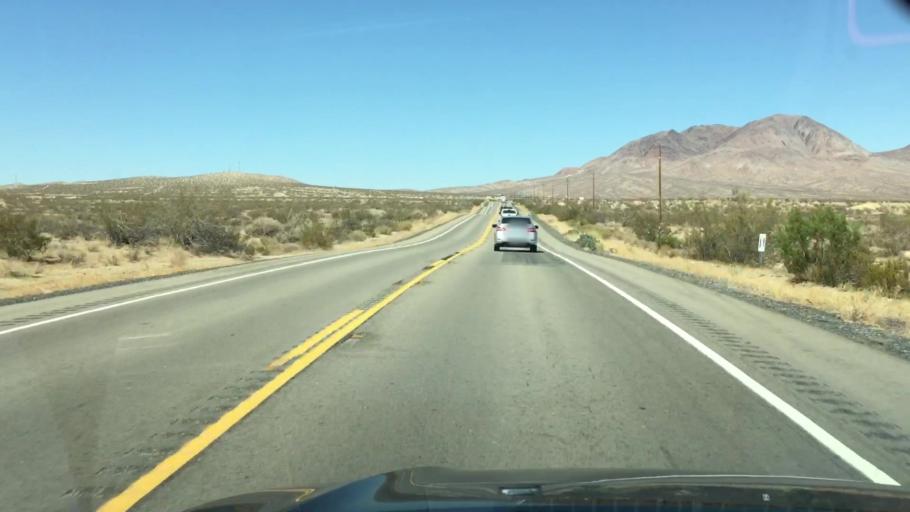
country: US
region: California
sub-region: Kern County
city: Boron
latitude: 35.2966
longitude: -117.6143
